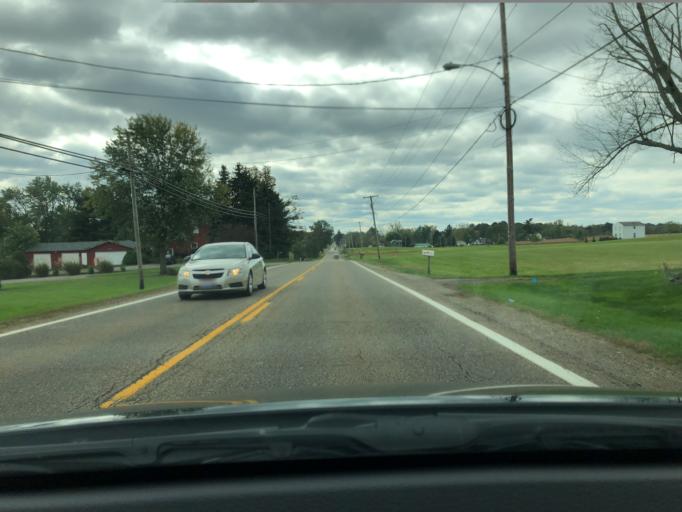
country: US
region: Ohio
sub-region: Stark County
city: Massillon
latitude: 40.8058
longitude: -81.6020
